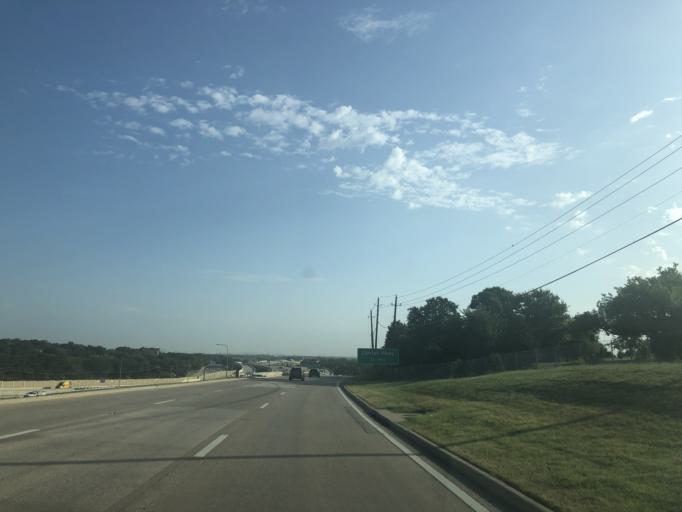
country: US
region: Texas
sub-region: Dallas County
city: Grand Prairie
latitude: 32.7654
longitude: -97.0283
